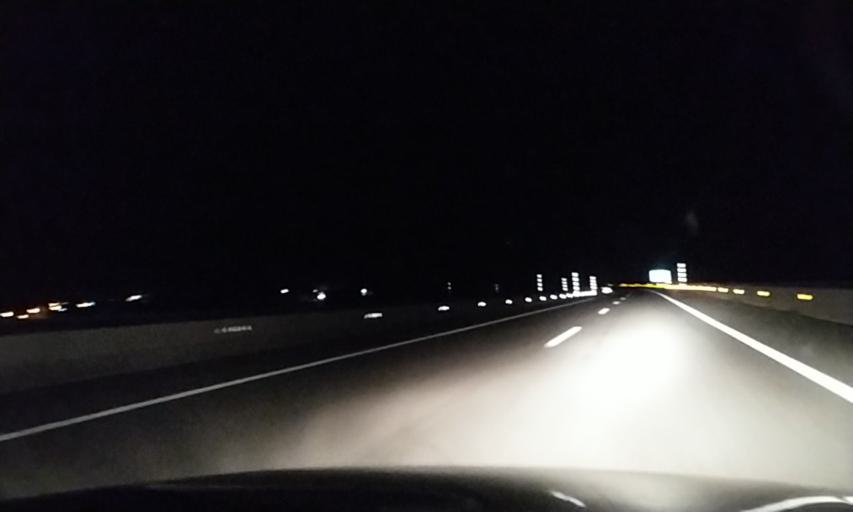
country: ES
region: Castille and Leon
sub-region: Provincia de Zamora
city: Puebla de Sanabria
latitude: 42.0604
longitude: -6.6157
